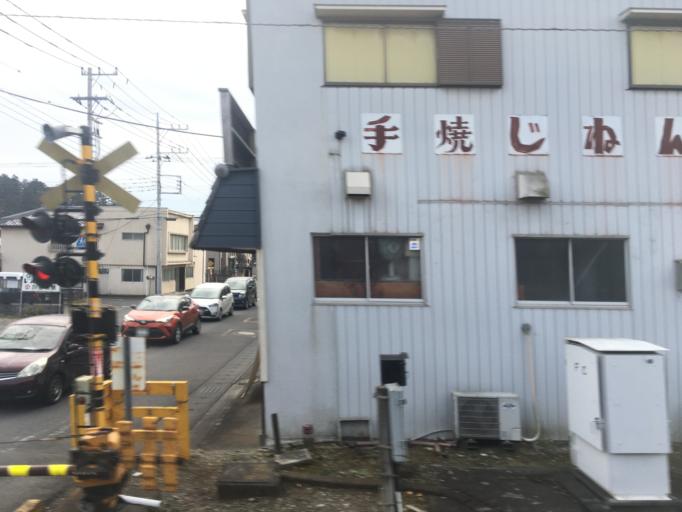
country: JP
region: Tochigi
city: Sano
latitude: 36.3168
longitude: 139.5847
